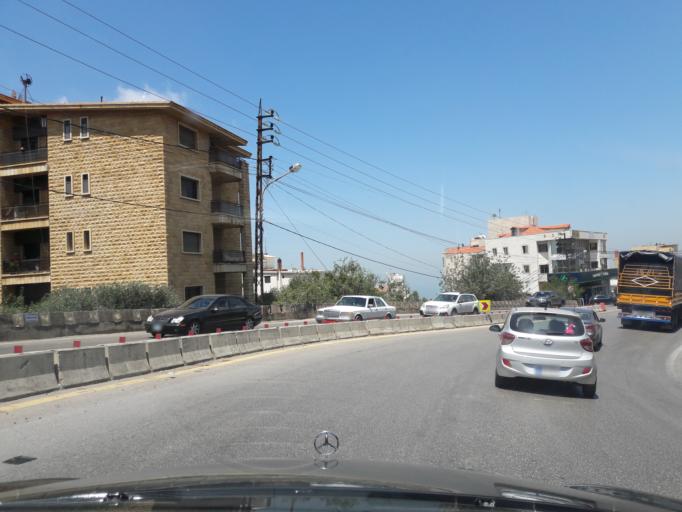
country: LB
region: Mont-Liban
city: Djounie
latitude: 33.9207
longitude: 35.6291
